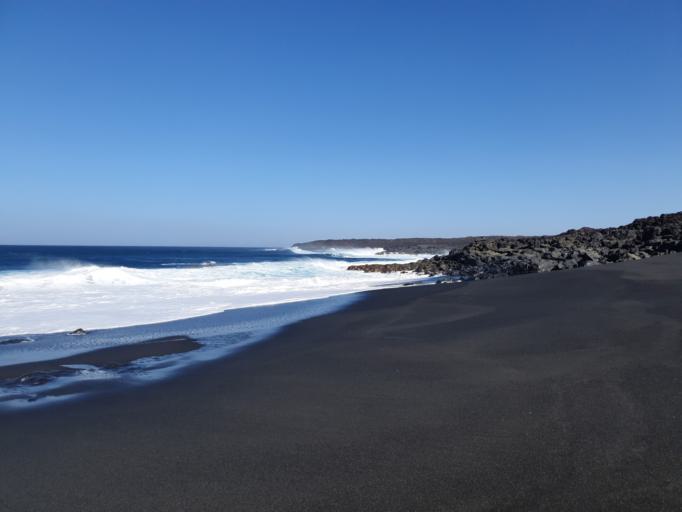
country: ES
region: Canary Islands
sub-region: Provincia de Las Palmas
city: Tinajo
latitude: 29.0660
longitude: -13.7630
